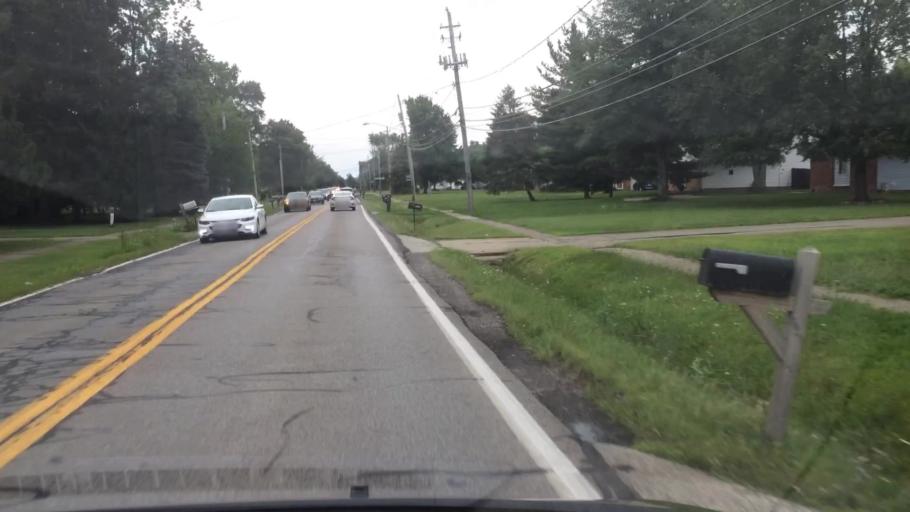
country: US
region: Ohio
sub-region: Cuyahoga County
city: Strongsville
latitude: 41.2995
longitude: -81.8111
